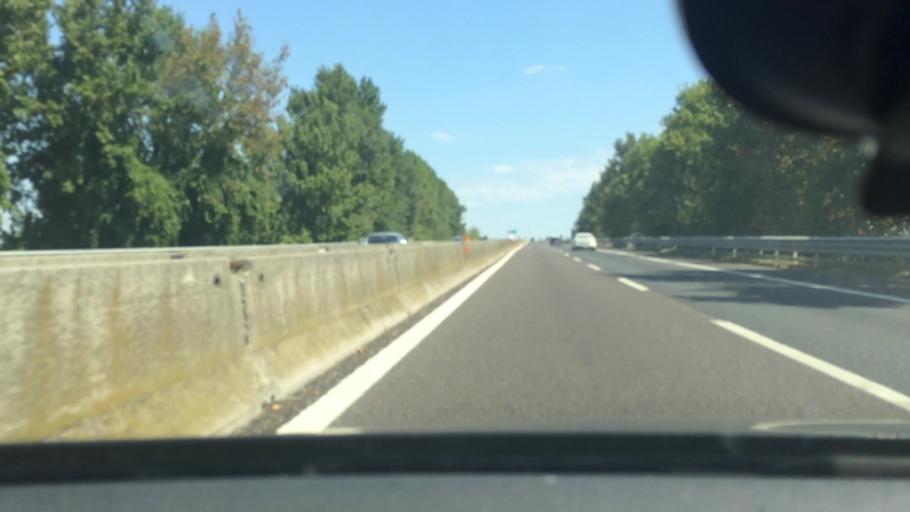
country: IT
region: Emilia-Romagna
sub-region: Provincia di Bologna
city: Malalbergo
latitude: 44.7299
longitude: 11.5137
